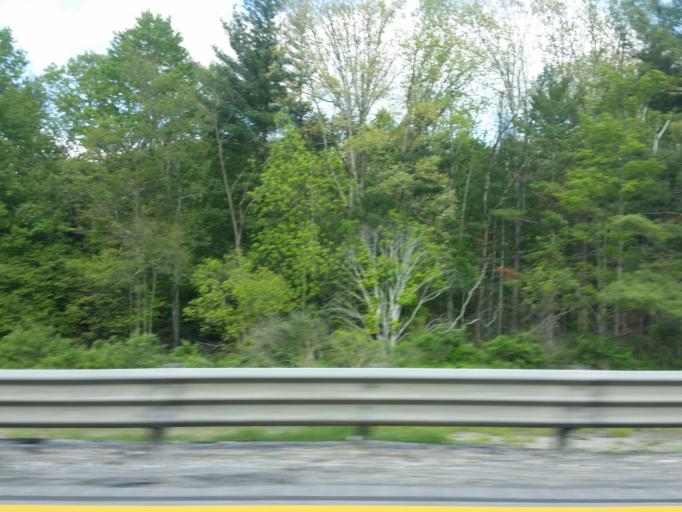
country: US
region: West Virginia
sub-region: Raleigh County
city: Beaver
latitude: 37.7084
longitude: -81.1520
